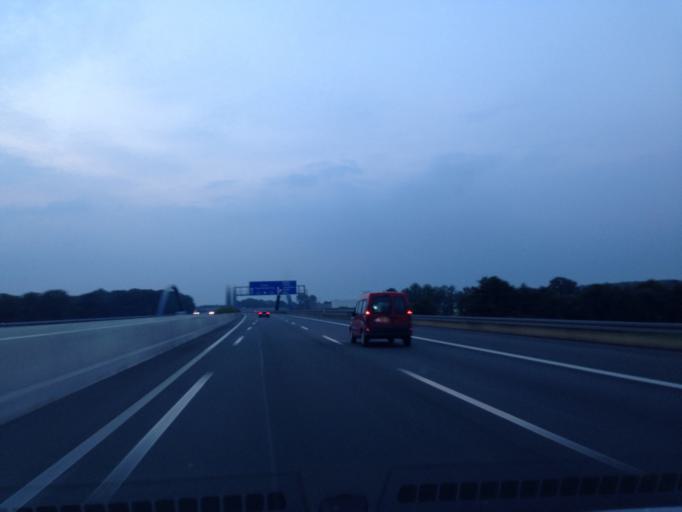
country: DE
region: North Rhine-Westphalia
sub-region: Regierungsbezirk Munster
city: Senden
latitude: 51.8766
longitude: 7.5764
